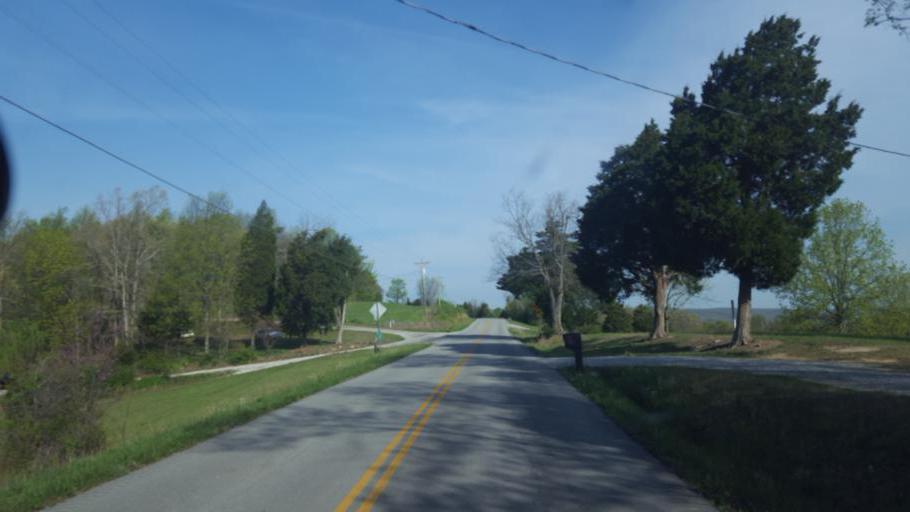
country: US
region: Kentucky
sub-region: Edmonson County
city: Brownsville
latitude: 37.3169
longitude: -86.1082
